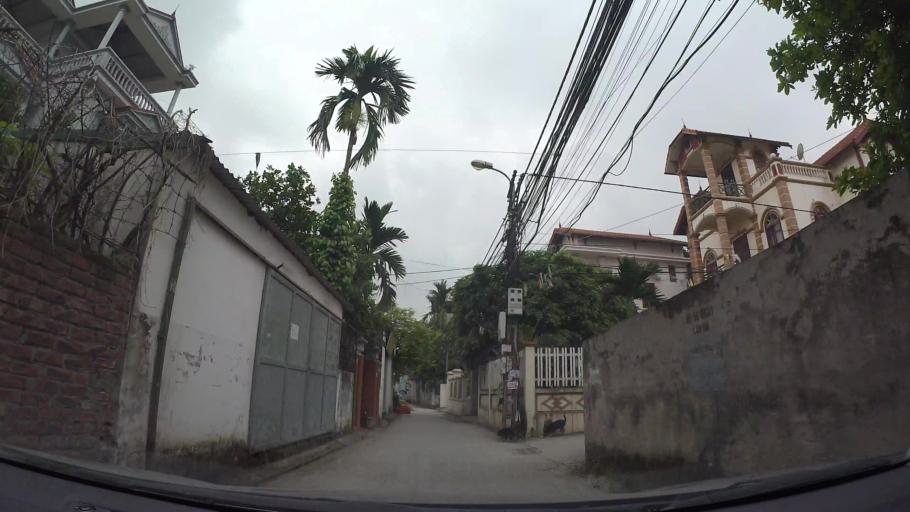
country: VN
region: Ha Noi
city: Trau Quy
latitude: 21.0708
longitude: 105.9191
